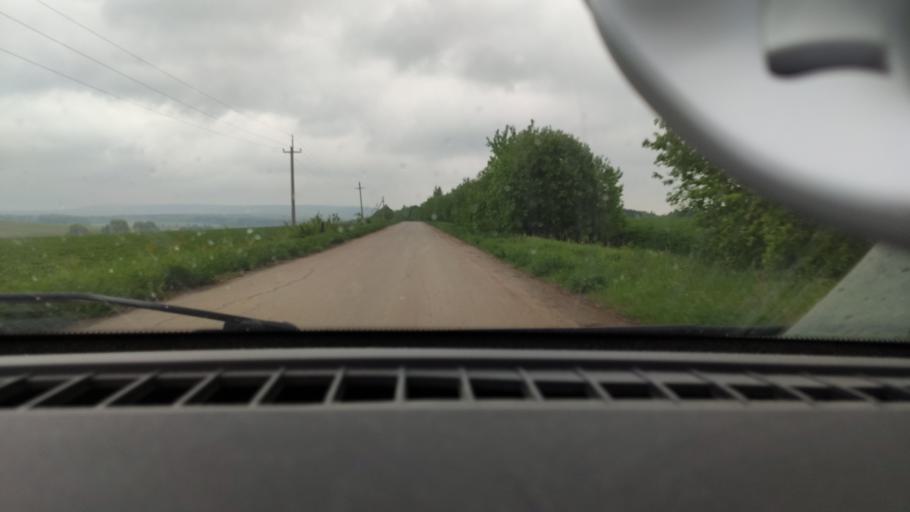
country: RU
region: Perm
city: Gamovo
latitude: 57.8561
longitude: 56.0819
